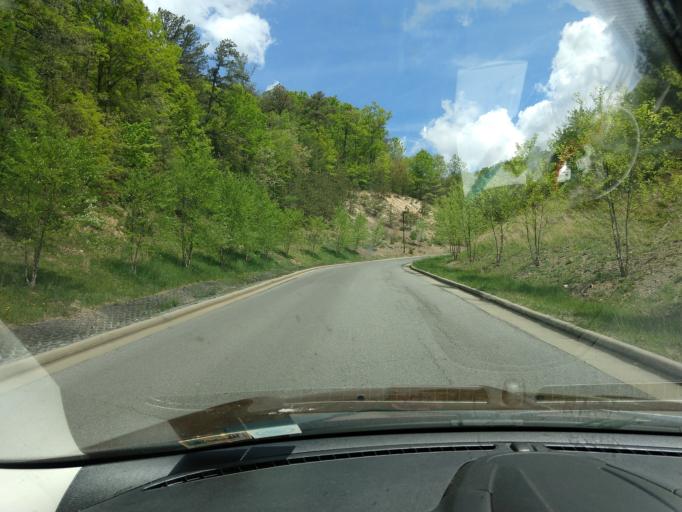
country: US
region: West Virginia
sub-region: Mercer County
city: Bluefield
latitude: 37.2546
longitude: -81.2394
